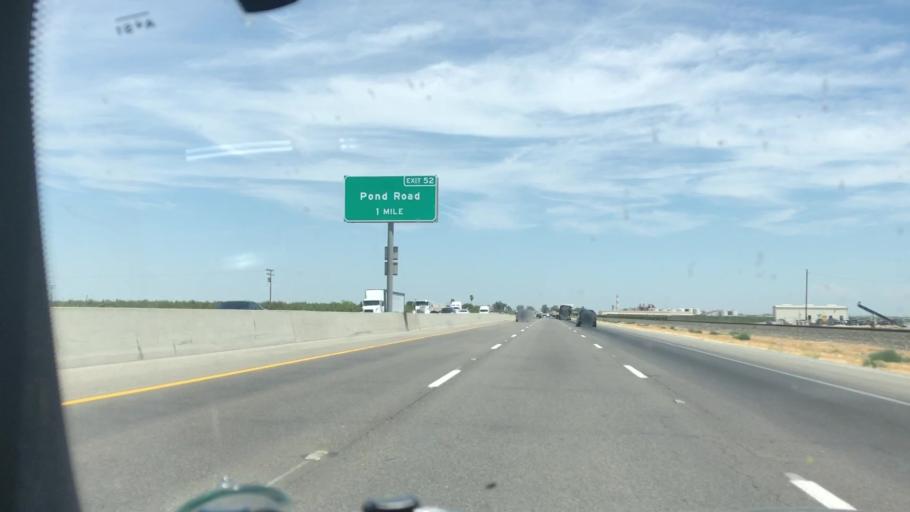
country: US
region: California
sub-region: Kern County
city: McFarland
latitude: 35.7019
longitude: -119.2327
